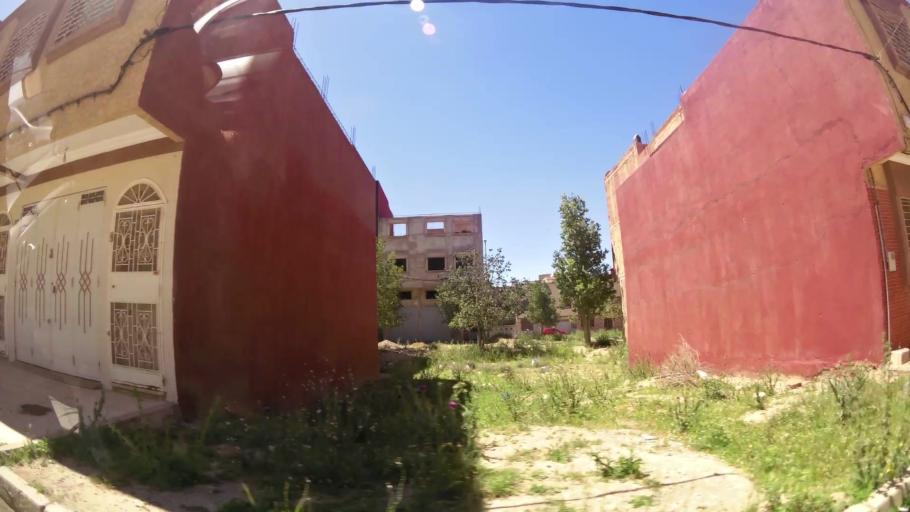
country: MA
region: Oriental
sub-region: Oujda-Angad
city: Oujda
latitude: 34.6799
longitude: -1.8655
